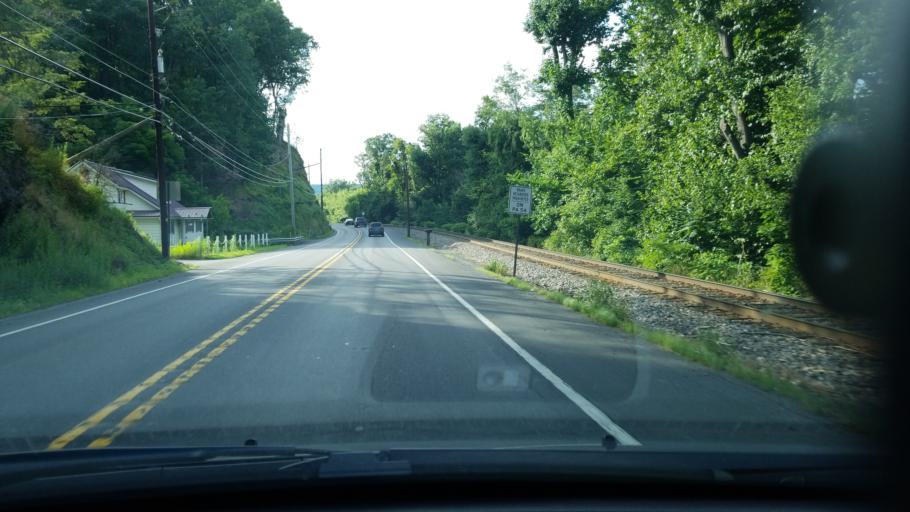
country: US
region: Pennsylvania
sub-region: Montour County
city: Danville
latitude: 40.9497
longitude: -76.6147
